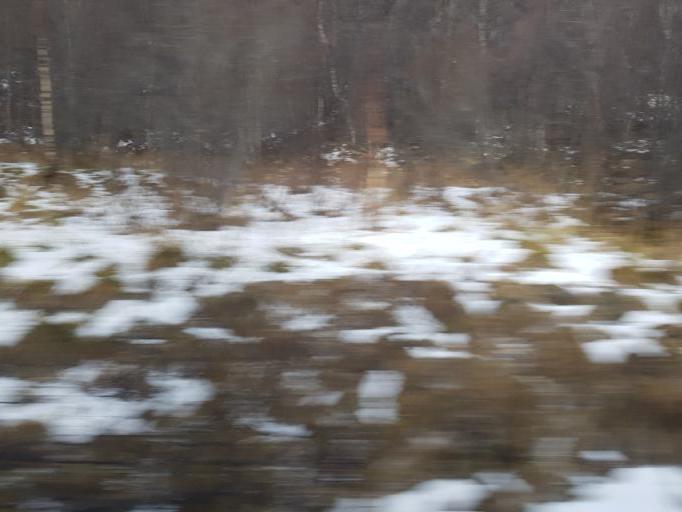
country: NO
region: Sor-Trondelag
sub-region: Oppdal
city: Oppdal
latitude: 62.3586
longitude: 9.6305
